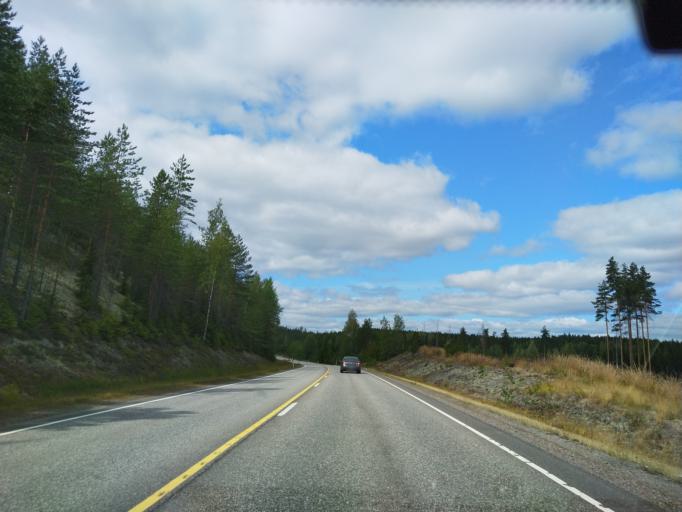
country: FI
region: Haeme
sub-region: Riihimaeki
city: Loppi
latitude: 60.7366
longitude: 24.3789
